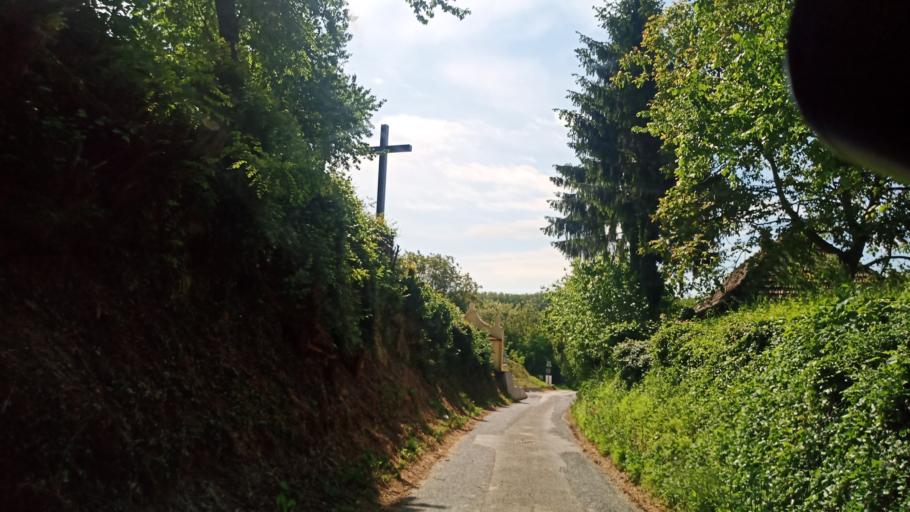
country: HU
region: Zala
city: Sarmellek
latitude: 46.6388
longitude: 17.1001
